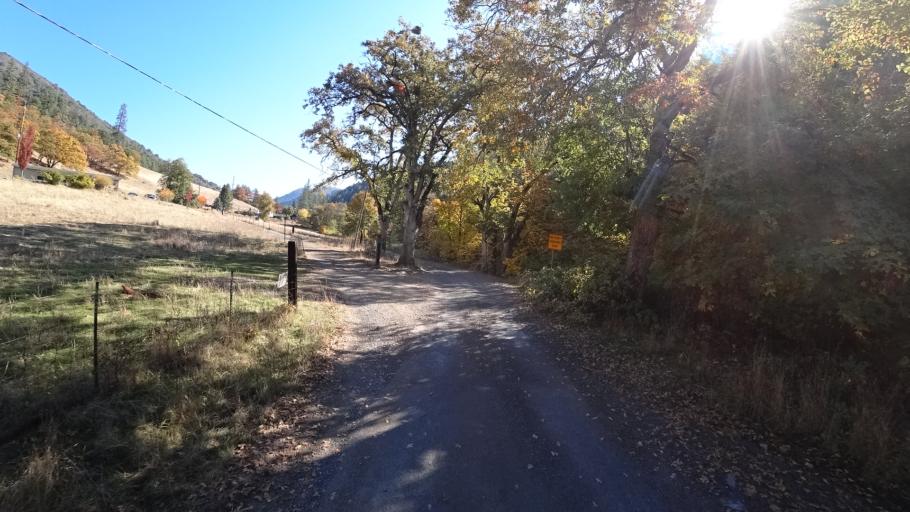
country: US
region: California
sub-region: Siskiyou County
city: Yreka
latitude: 41.7422
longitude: -122.9805
